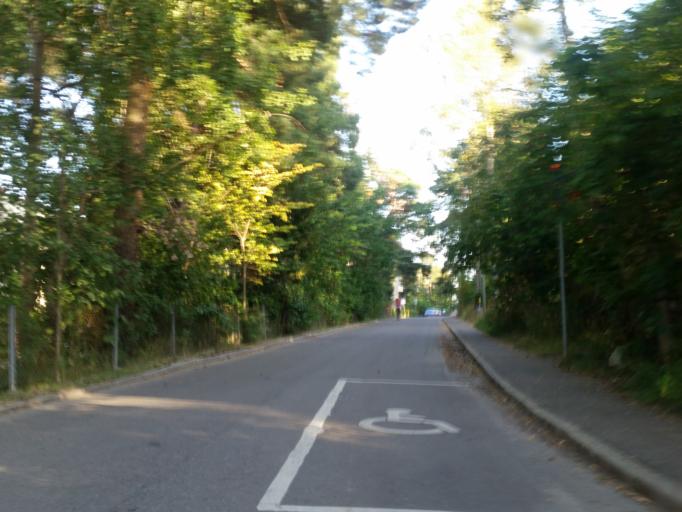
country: SE
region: Stockholm
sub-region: Sundbybergs Kommun
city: Sundbyberg
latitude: 59.3316
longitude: 17.9793
